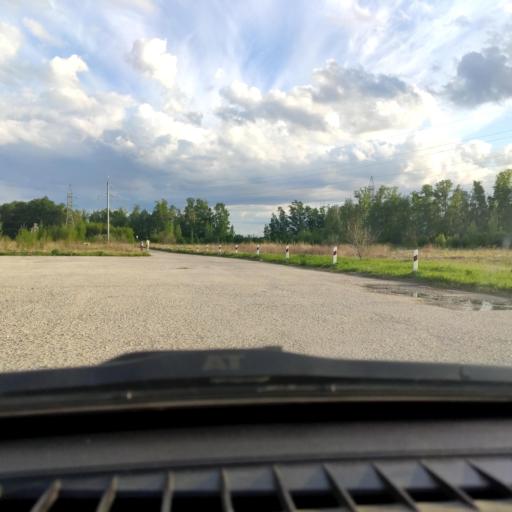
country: RU
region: Samara
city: Tol'yatti
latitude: 53.6185
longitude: 49.3134
